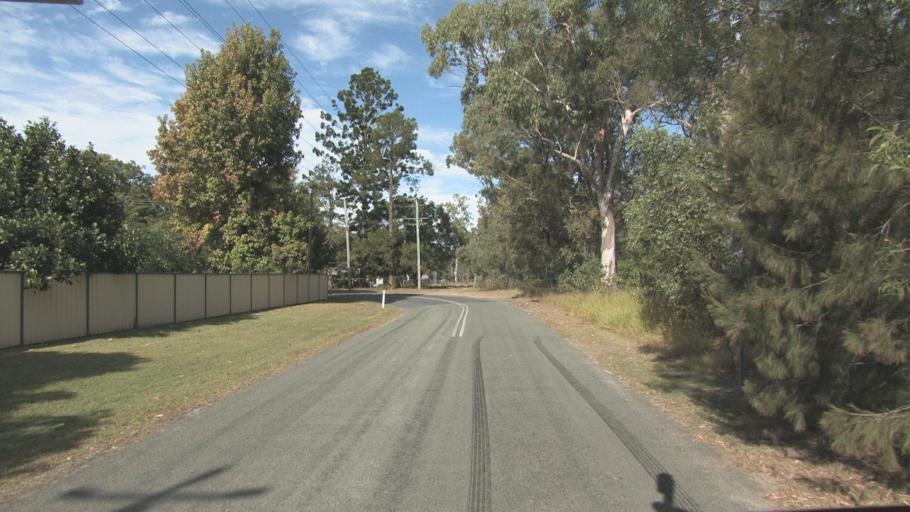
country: AU
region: Queensland
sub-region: Brisbane
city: Forest Lake
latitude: -27.6567
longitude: 152.9826
